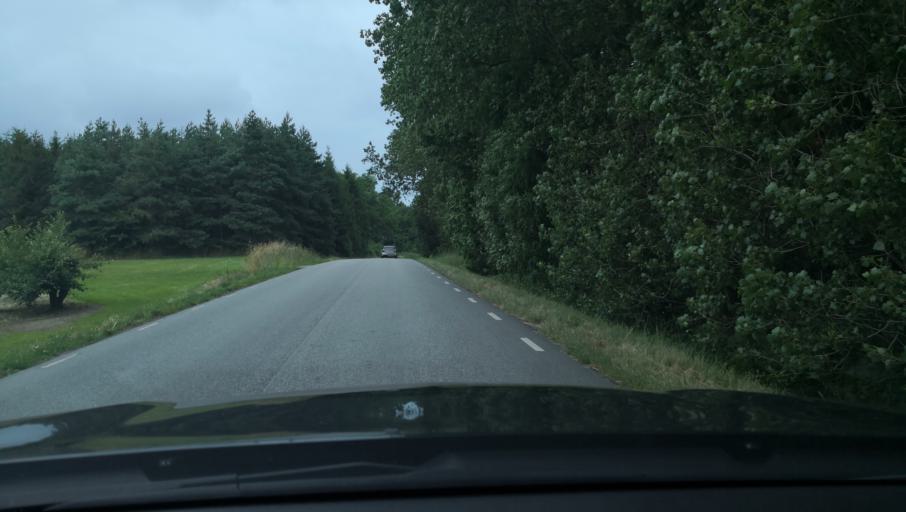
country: SE
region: Skane
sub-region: Simrishamns Kommun
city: Kivik
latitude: 55.6712
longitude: 14.2179
